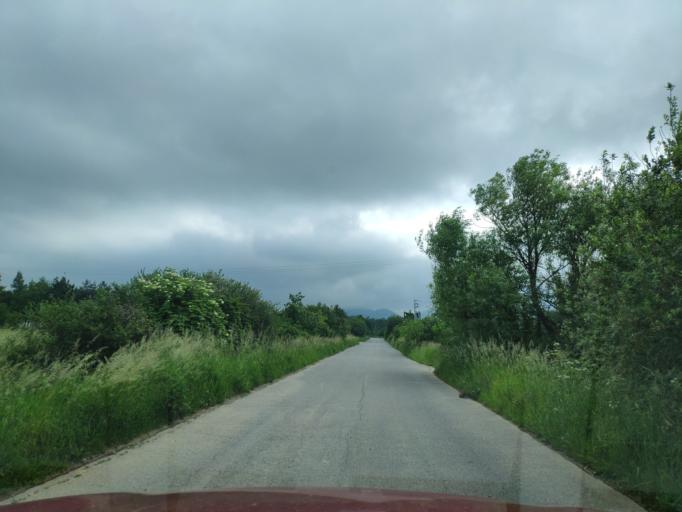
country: SK
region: Presovsky
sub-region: Okres Presov
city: Presov
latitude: 48.9970
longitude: 21.2990
